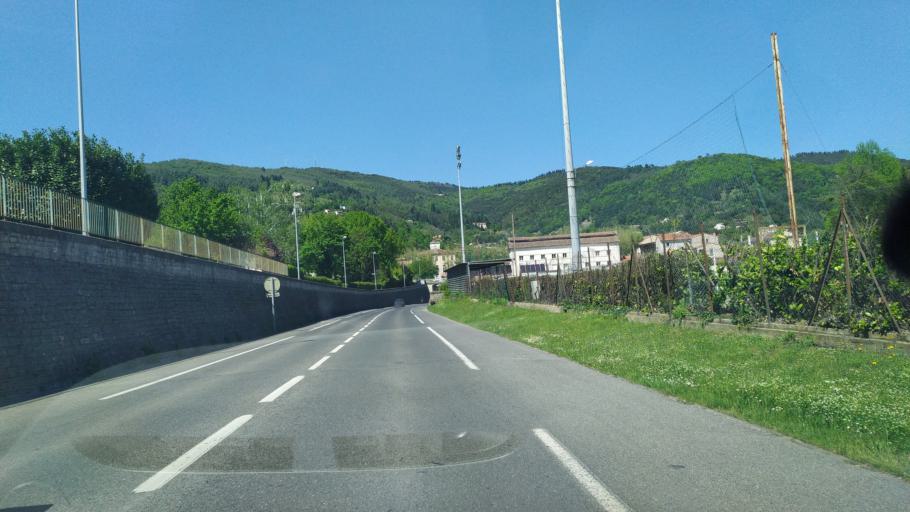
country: FR
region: Languedoc-Roussillon
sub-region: Departement du Gard
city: Le Vigan
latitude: 43.9866
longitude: 3.6046
